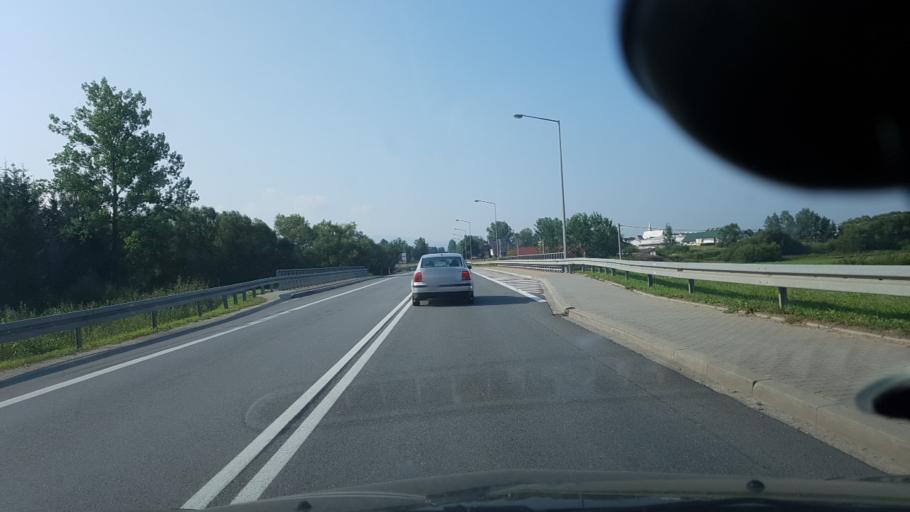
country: PL
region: Lesser Poland Voivodeship
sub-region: Powiat nowotarski
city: Jablonka
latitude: 49.4684
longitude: 19.6924
